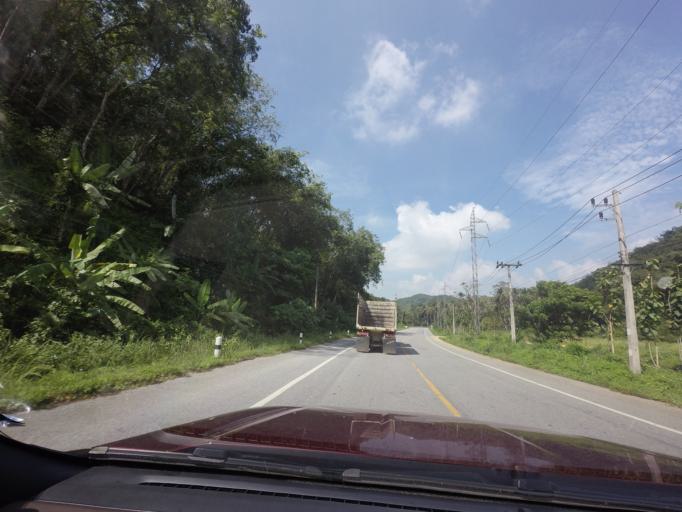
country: TH
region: Yala
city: Betong
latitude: 5.8510
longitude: 101.1151
